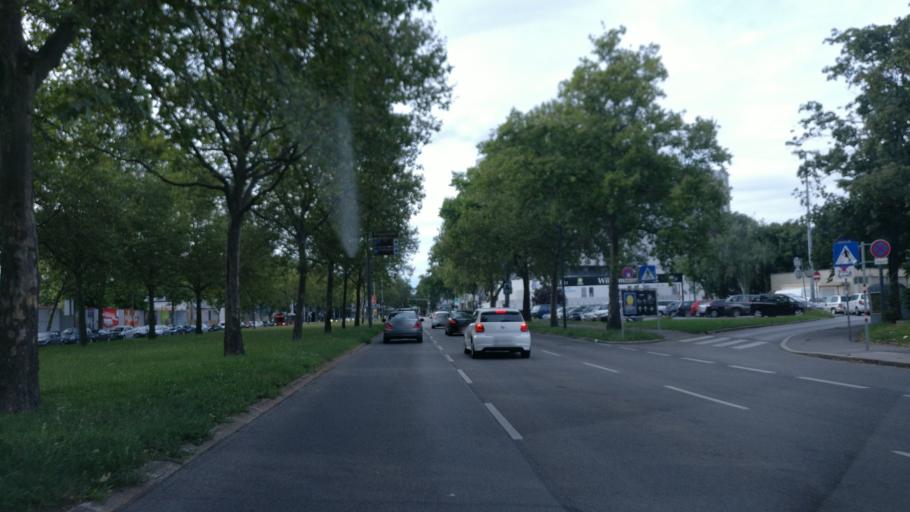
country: AT
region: Lower Austria
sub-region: Politischer Bezirk Wien-Umgebung
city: Gerasdorf bei Wien
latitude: 48.2402
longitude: 16.4368
